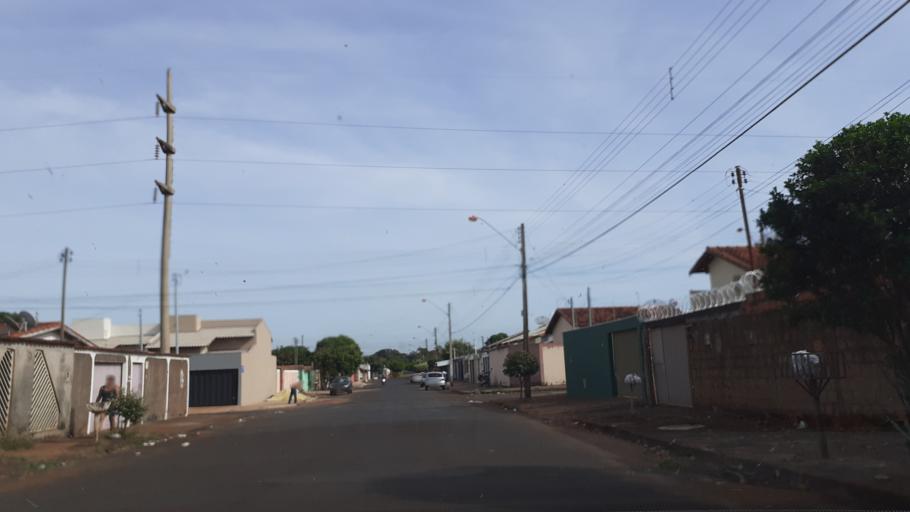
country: BR
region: Goias
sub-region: Itumbiara
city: Itumbiara
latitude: -18.4221
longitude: -49.2485
